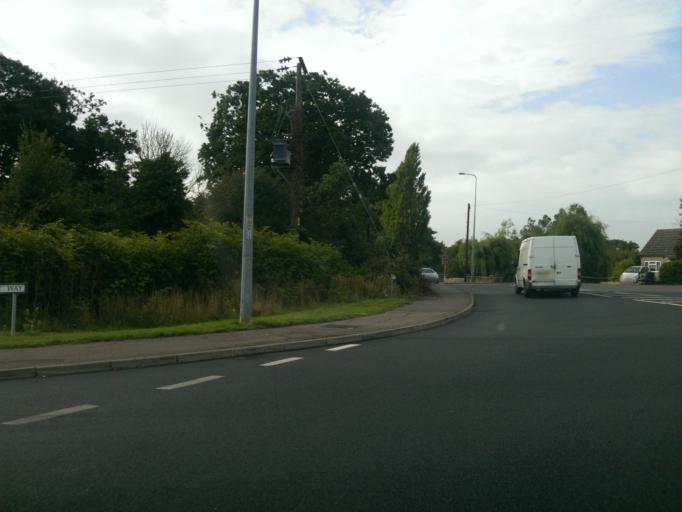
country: GB
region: England
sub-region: Essex
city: Little Clacton
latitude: 51.8203
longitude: 1.1418
